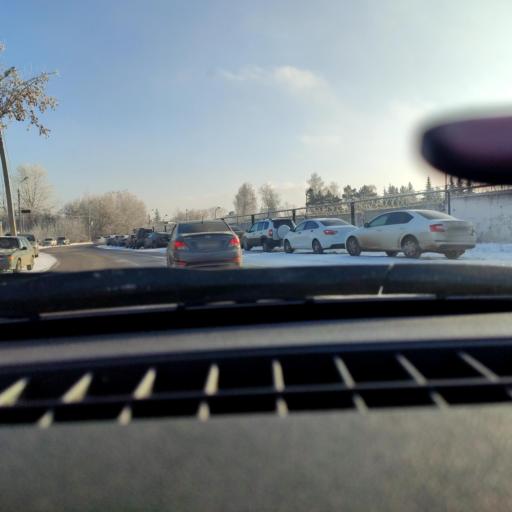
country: RU
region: Bashkortostan
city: Ufa
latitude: 54.8055
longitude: 56.0716
